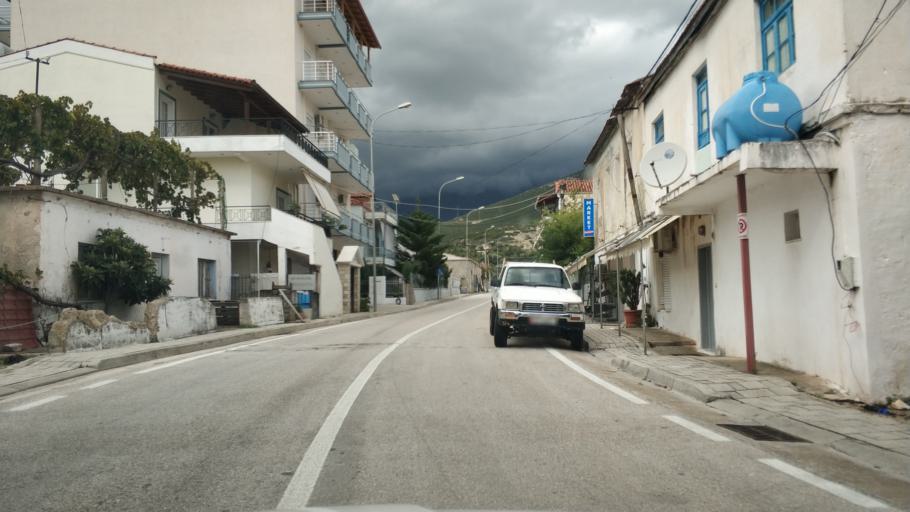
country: AL
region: Vlore
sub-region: Rrethi i Vlores
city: Himare
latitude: 40.1058
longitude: 19.7424
